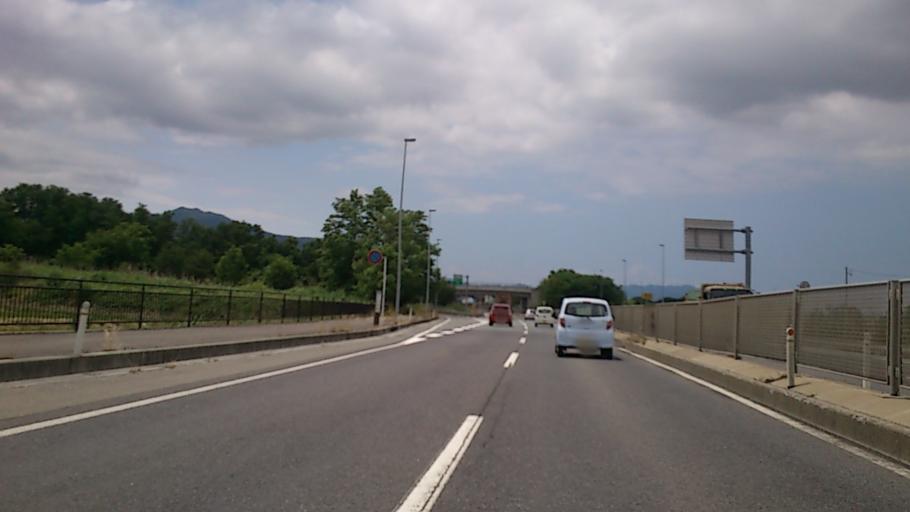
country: JP
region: Yamagata
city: Kaminoyama
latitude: 38.1903
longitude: 140.3111
